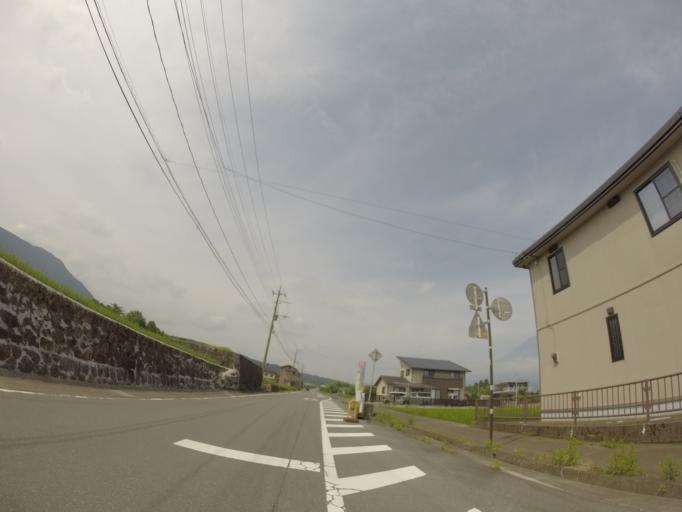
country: JP
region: Shizuoka
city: Fujinomiya
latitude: 35.2815
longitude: 138.5750
